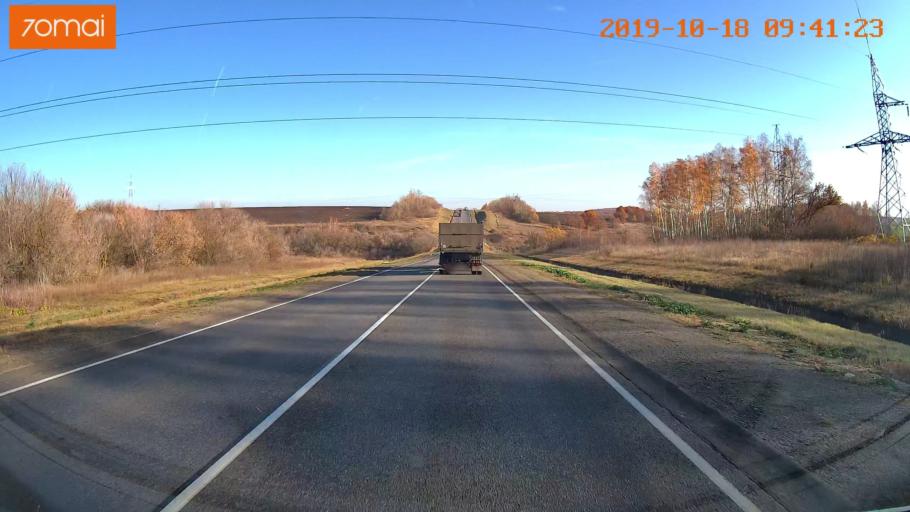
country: RU
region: Tula
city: Kazachka
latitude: 53.2743
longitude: 38.1610
